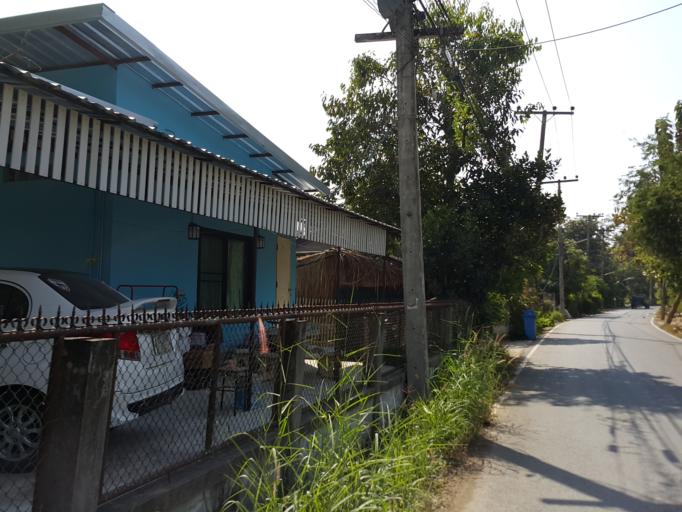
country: TH
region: Chiang Mai
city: San Kamphaeng
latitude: 18.7615
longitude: 99.0959
